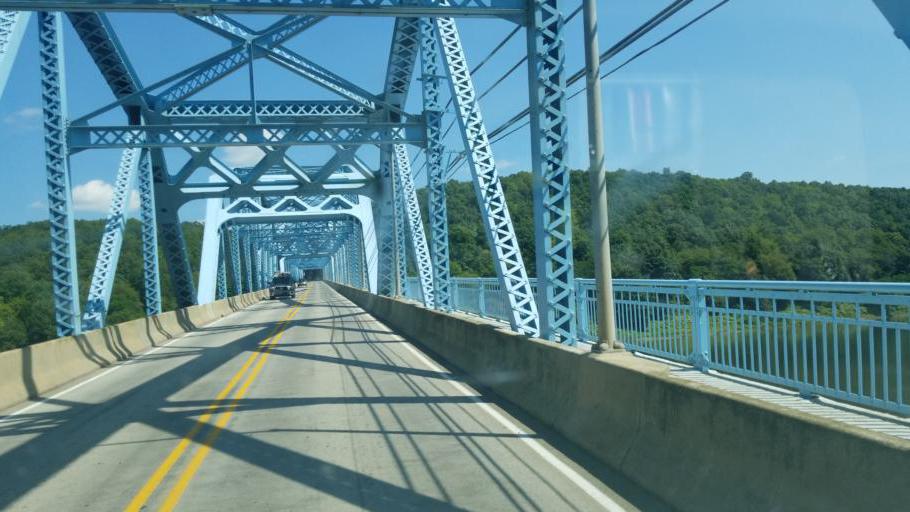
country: US
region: Pennsylvania
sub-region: Butler County
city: Chicora
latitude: 41.1020
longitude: -79.6808
